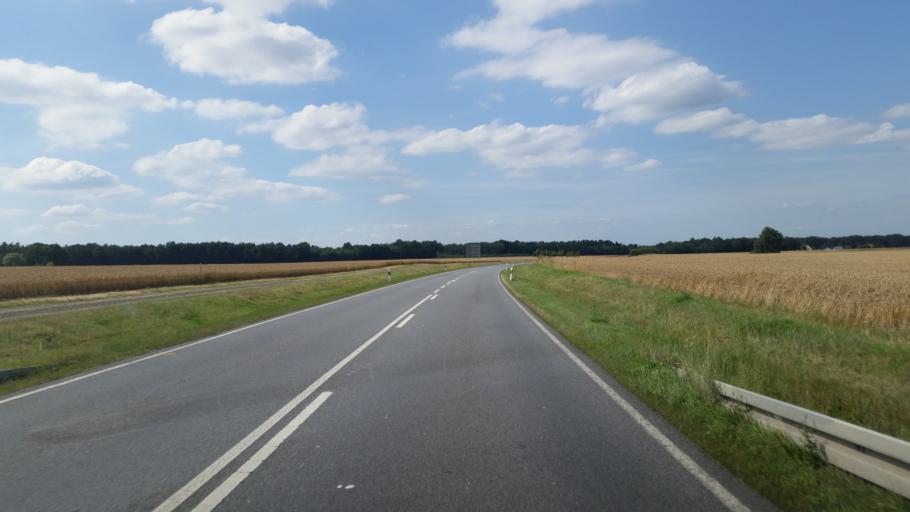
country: DE
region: Saxony
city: Nebelschutz
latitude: 51.2657
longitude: 14.1447
